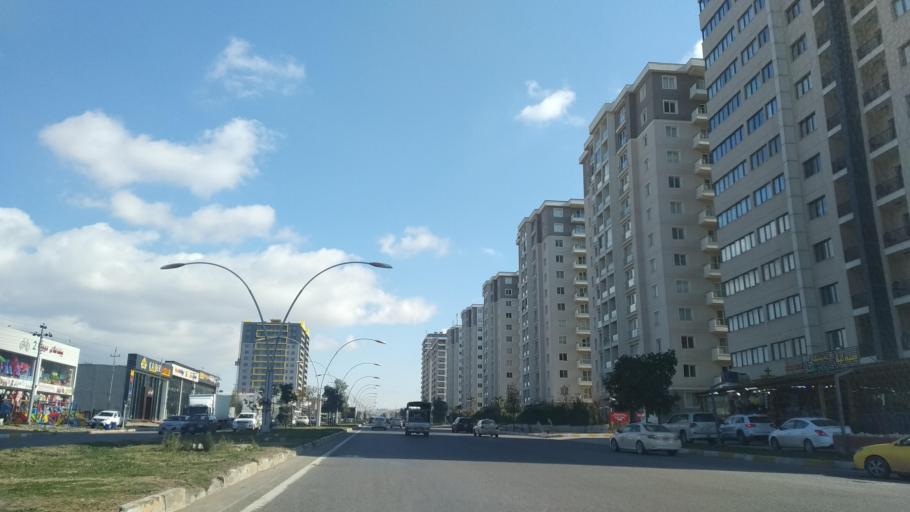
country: IQ
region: Arbil
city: Erbil
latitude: 36.2046
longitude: 44.1168
